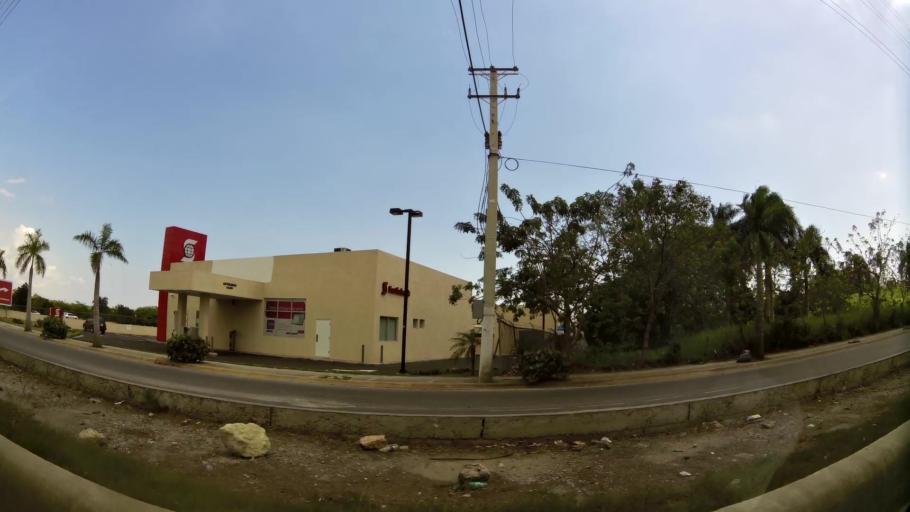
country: DO
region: Nacional
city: Santo Domingo
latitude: 18.5085
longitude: -69.9691
